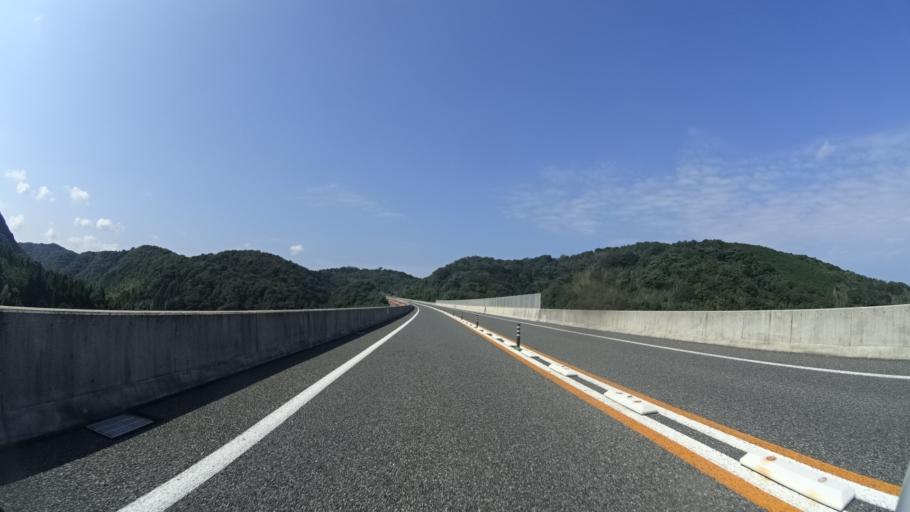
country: JP
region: Shimane
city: Gotsucho
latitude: 34.9692
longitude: 132.1727
